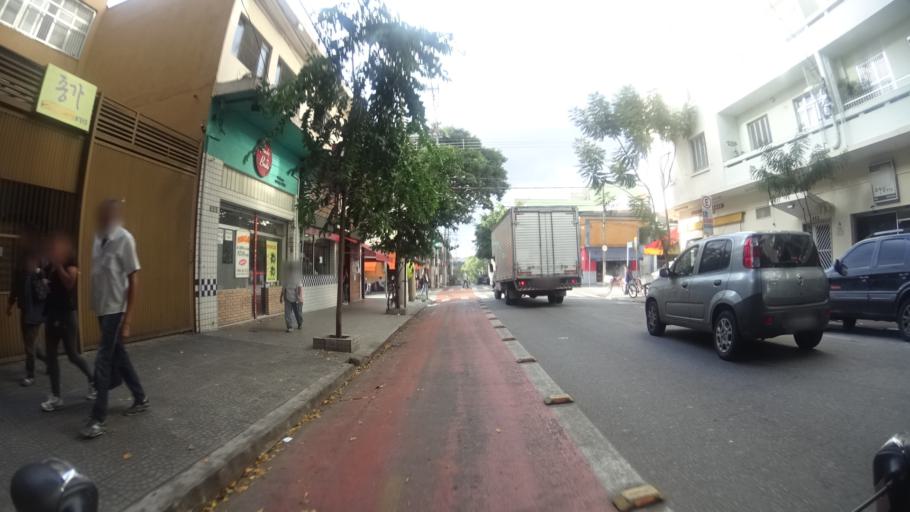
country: BR
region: Sao Paulo
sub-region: Sao Paulo
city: Sao Paulo
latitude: -23.5288
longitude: -46.6357
